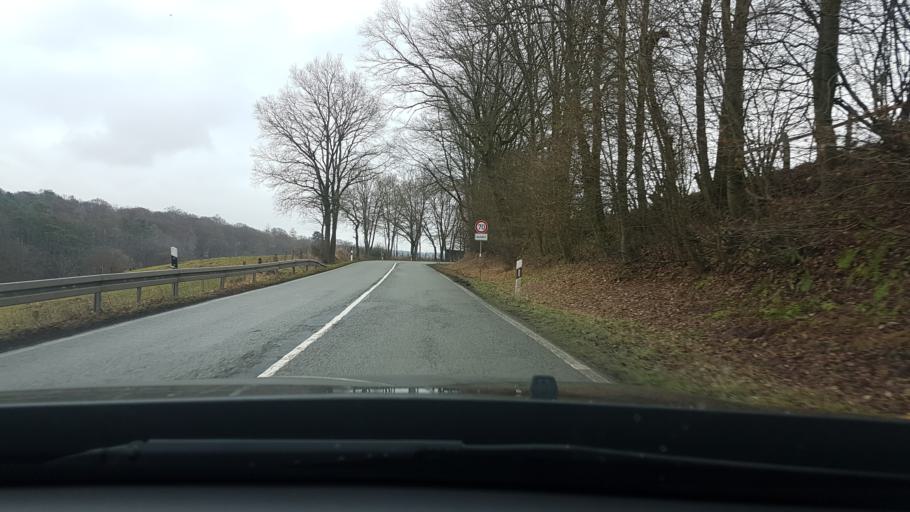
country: DE
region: Hesse
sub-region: Regierungsbezirk Kassel
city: Bad Arolsen
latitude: 51.4996
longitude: 9.0032
